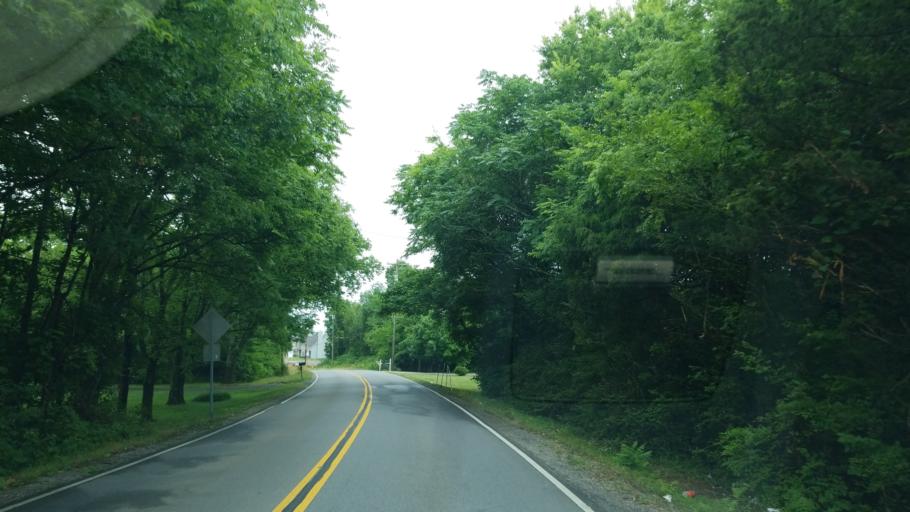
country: US
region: Tennessee
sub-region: Rutherford County
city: La Vergne
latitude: 36.0575
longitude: -86.5952
